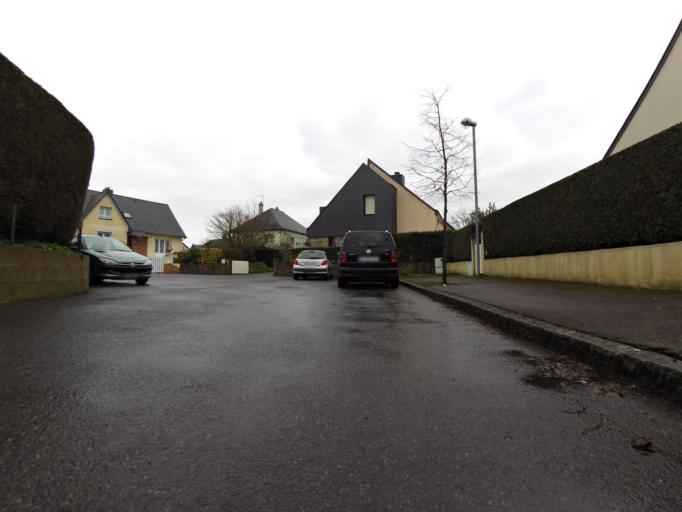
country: FR
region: Brittany
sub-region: Departement d'Ille-et-Vilaine
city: Laille
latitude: 47.9787
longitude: -1.7234
